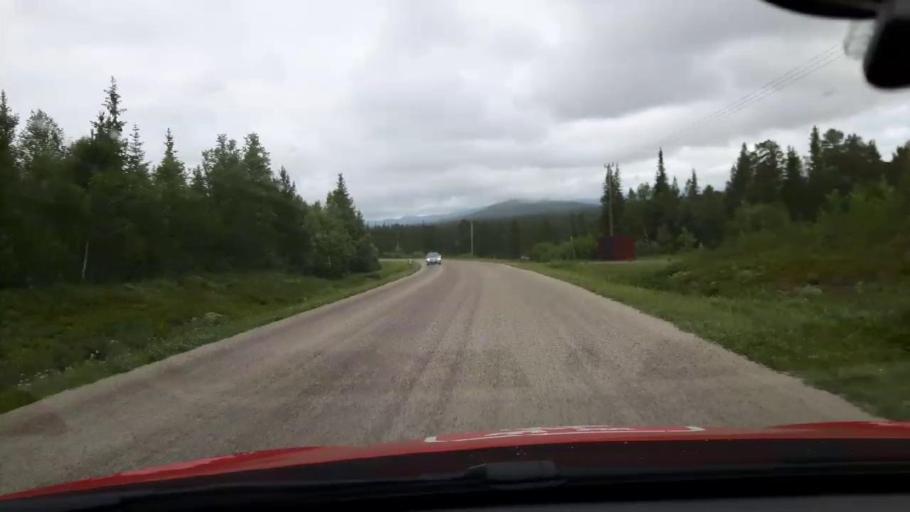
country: NO
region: Nord-Trondelag
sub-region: Meraker
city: Meraker
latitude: 63.2701
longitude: 12.3710
